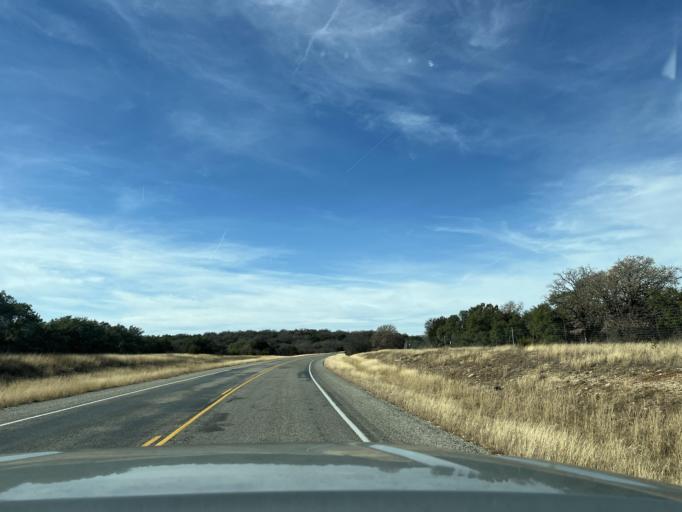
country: US
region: Texas
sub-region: Eastland County
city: Cisco
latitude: 32.4609
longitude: -99.0108
